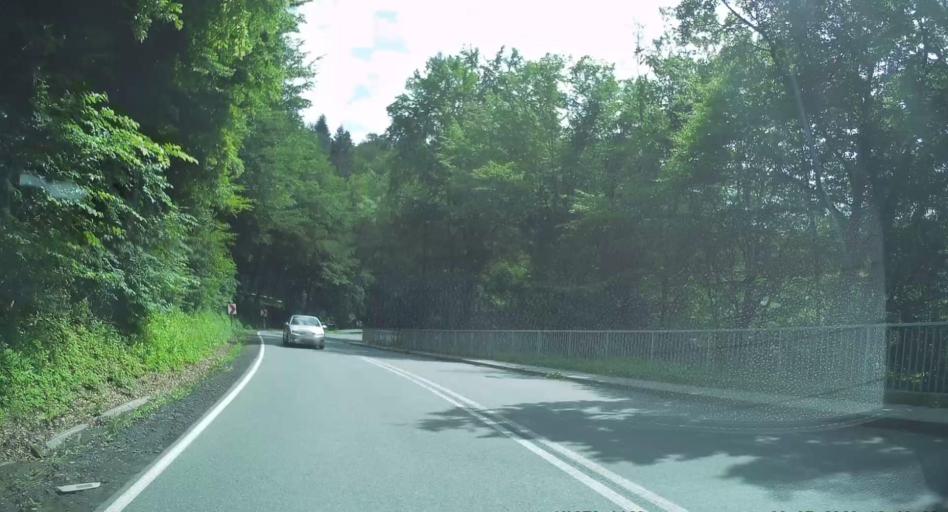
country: PL
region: Lesser Poland Voivodeship
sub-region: Powiat nowosadecki
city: Muszyna
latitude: 49.3534
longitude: 20.8118
